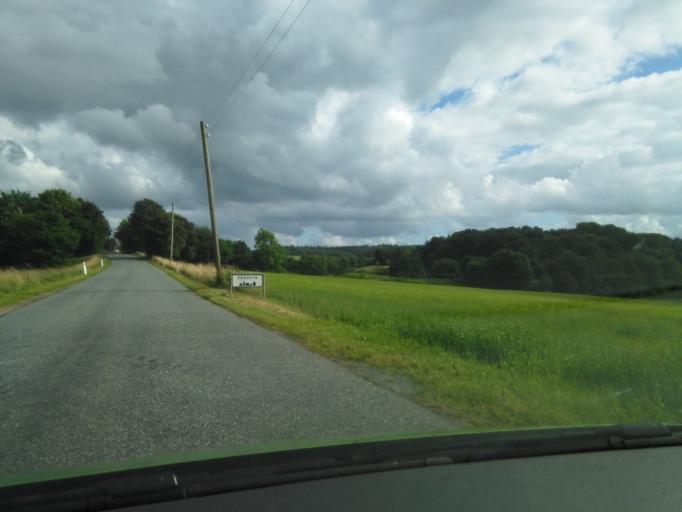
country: DK
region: Central Jutland
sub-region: Horsens Kommune
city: Braedstrup
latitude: 55.9696
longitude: 9.7093
